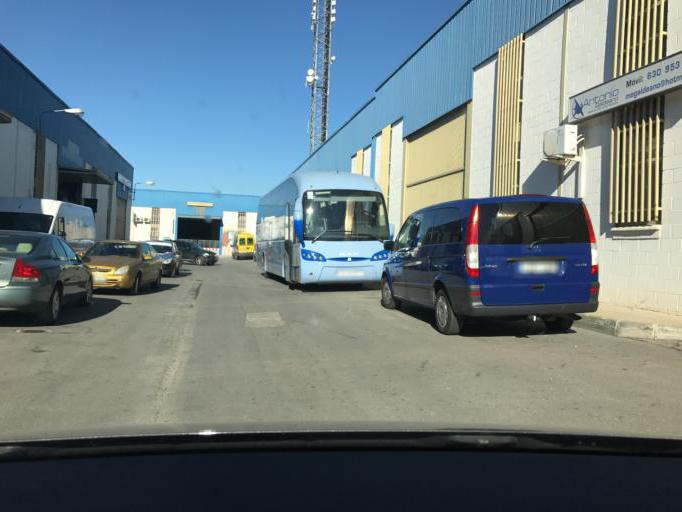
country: ES
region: Andalusia
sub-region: Provincia de Granada
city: Peligros
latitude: 37.2254
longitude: -3.6369
